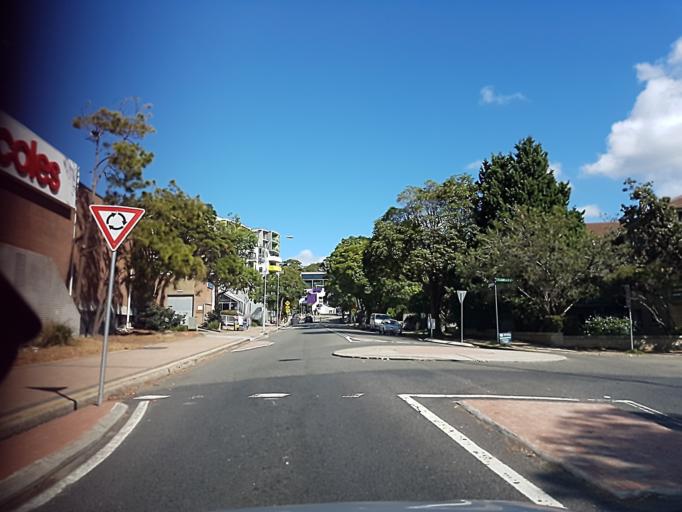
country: AU
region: New South Wales
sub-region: Warringah
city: Dee Why
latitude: -33.7519
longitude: 151.2901
